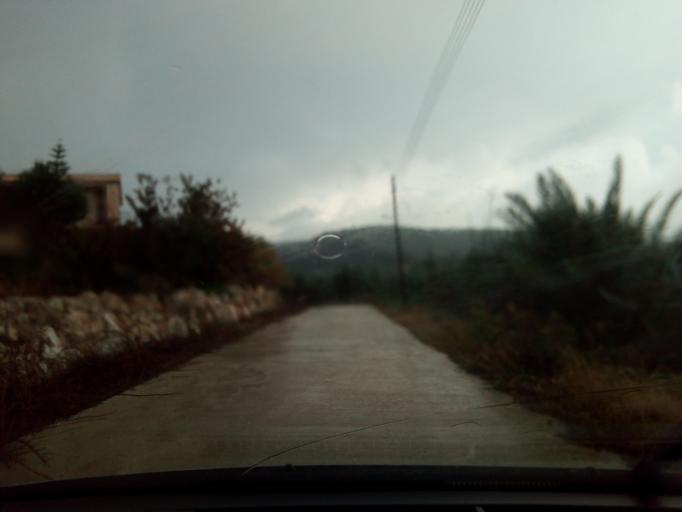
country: CY
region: Pafos
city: Polis
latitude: 34.9887
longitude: 32.4724
